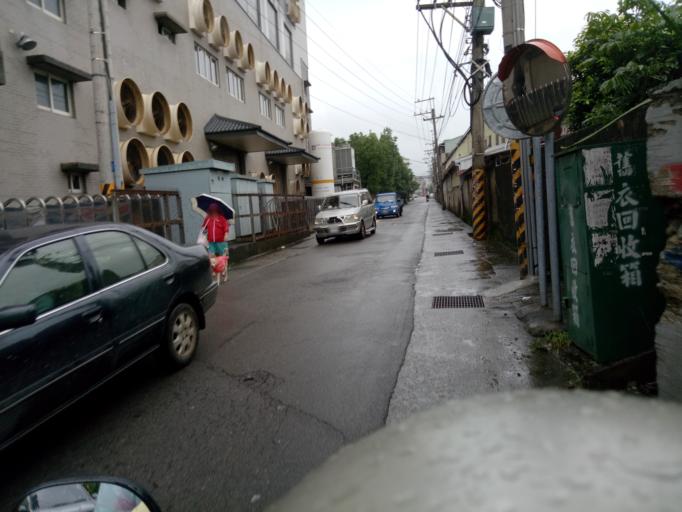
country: TW
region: Taiwan
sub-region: Taichung City
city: Taichung
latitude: 24.1039
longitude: 120.7184
